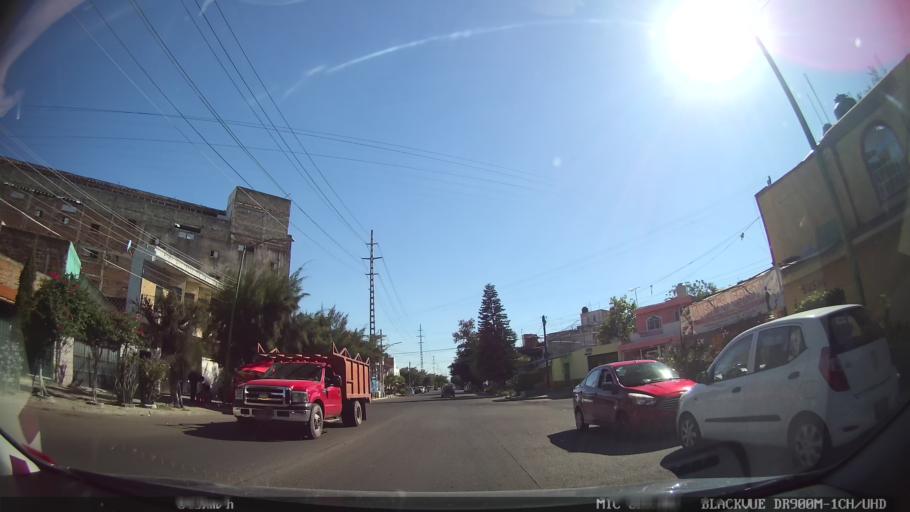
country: MX
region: Jalisco
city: Tlaquepaque
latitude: 20.6668
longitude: -103.2862
